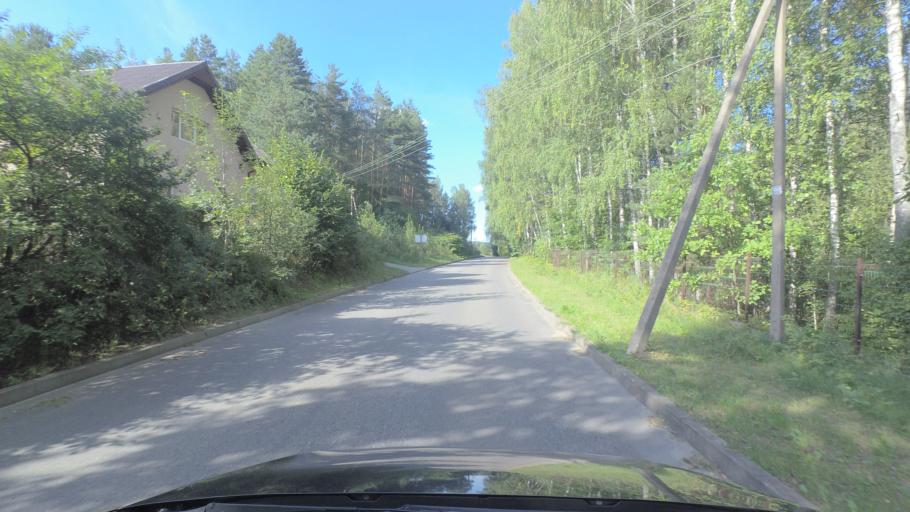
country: LT
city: Nemencine
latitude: 54.8429
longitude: 25.3715
